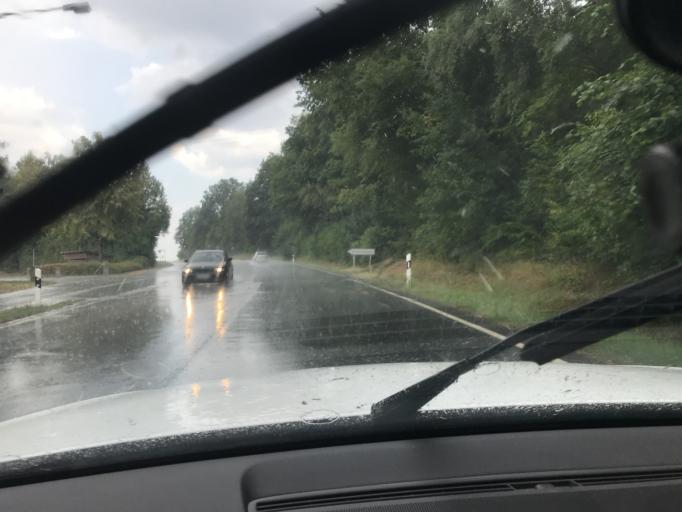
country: DE
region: Bavaria
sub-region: Upper Palatinate
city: Speinshart
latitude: 49.7508
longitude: 11.8365
